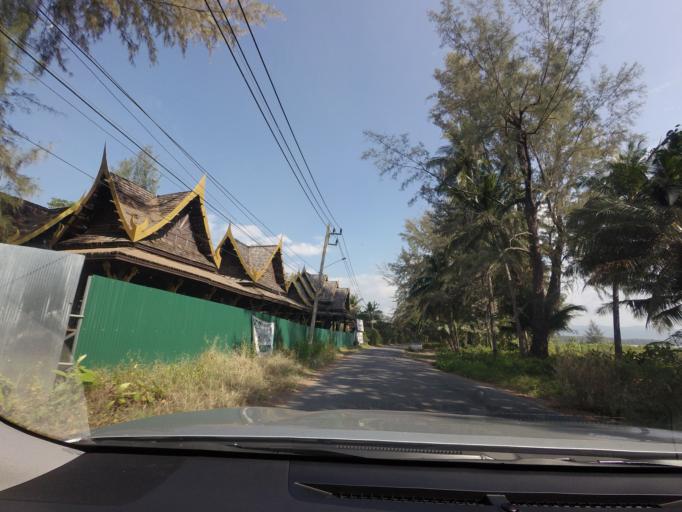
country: TH
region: Phangnga
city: Ban Khao Lak
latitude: 8.7265
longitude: 98.2285
